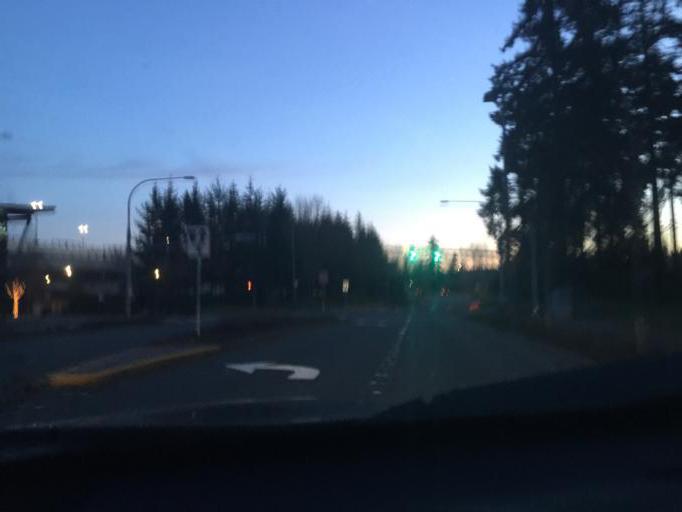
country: US
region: Washington
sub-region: King County
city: Redmond
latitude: 47.6712
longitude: -122.1244
